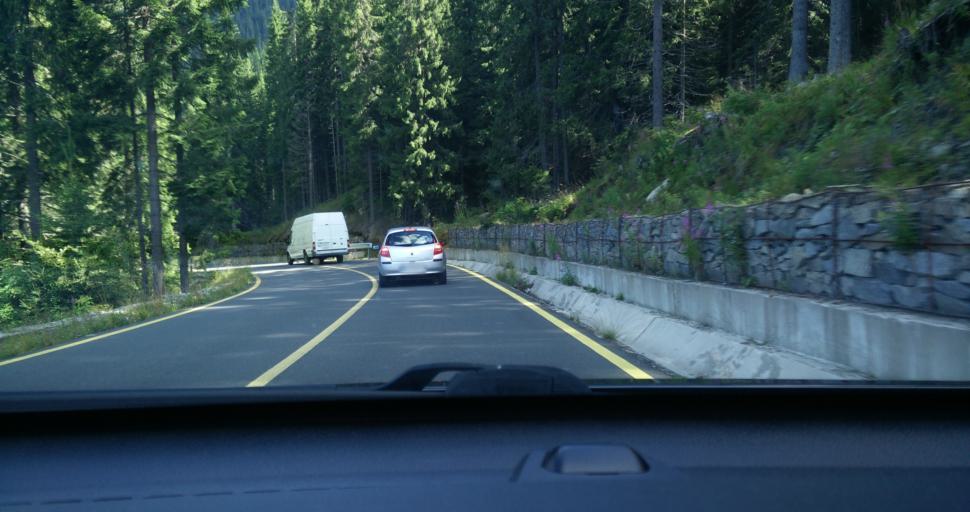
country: RO
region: Gorj
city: Novaci-Straini
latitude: 45.3944
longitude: 23.6323
